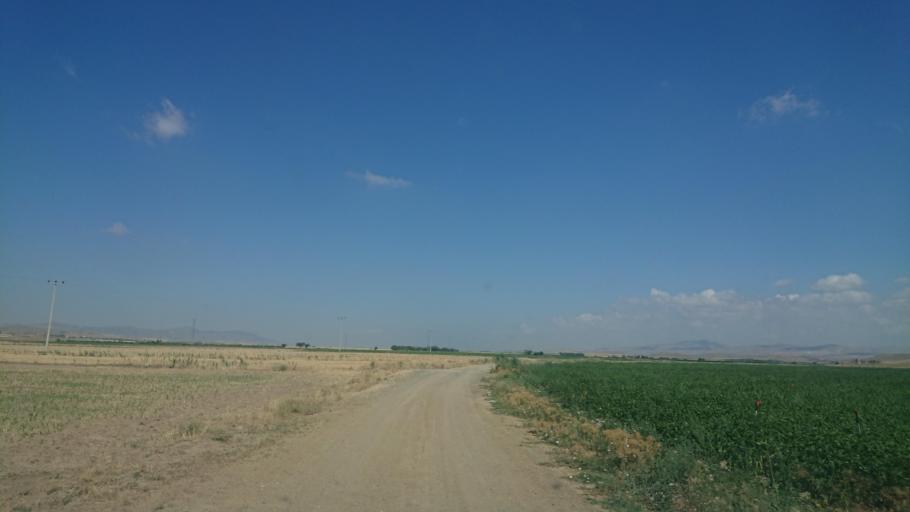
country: TR
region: Aksaray
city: Sariyahsi
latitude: 38.9768
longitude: 33.9121
